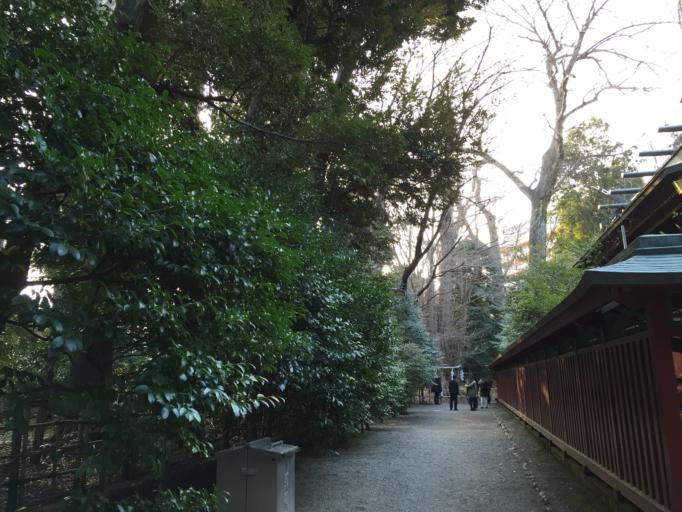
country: JP
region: Tokyo
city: Kokubunji
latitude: 35.6673
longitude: 139.4792
